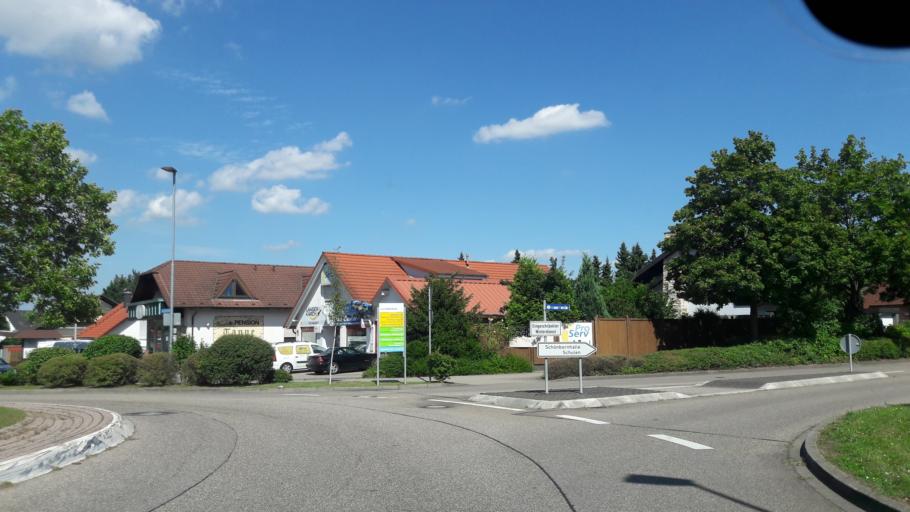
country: DE
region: Baden-Wuerttemberg
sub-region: Karlsruhe Region
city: Kronau
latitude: 49.2147
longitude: 8.6522
